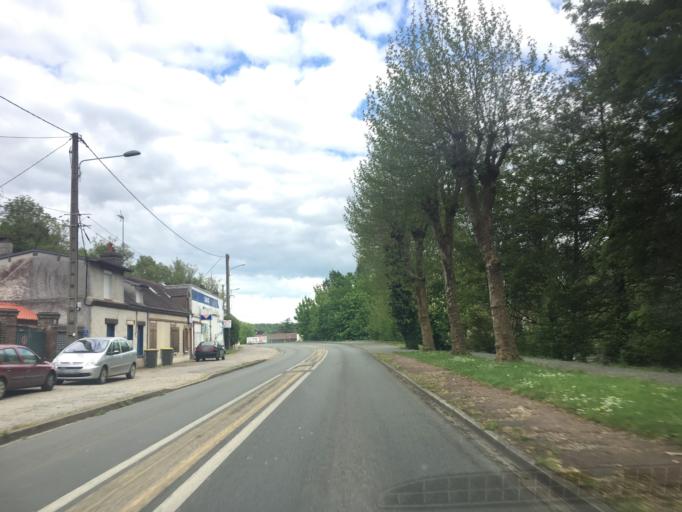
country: FR
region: Centre
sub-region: Departement d'Eure-et-Loir
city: Saint-Lubin-des-Joncherets
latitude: 48.7658
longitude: 1.2095
